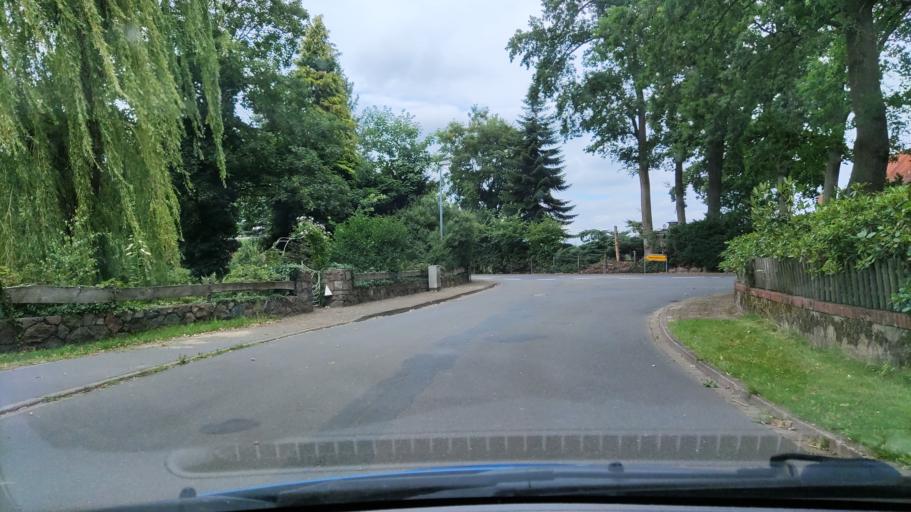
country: DE
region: Lower Saxony
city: Weste
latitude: 53.0604
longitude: 10.7029
